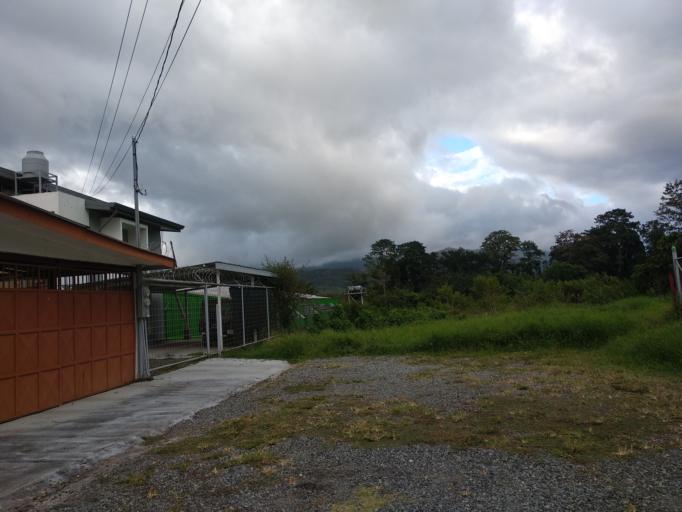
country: CR
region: Cartago
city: Turrialba
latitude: 9.8994
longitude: -83.6722
